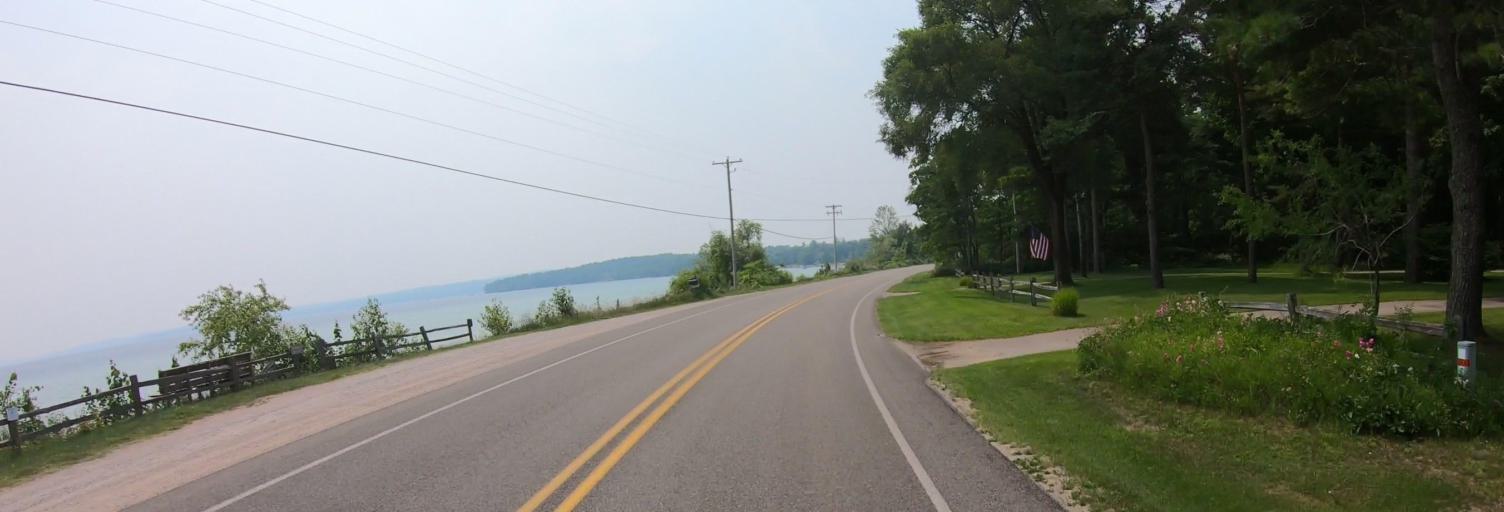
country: US
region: Michigan
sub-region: Leelanau County
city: Leland
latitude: 45.1528
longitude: -85.5932
